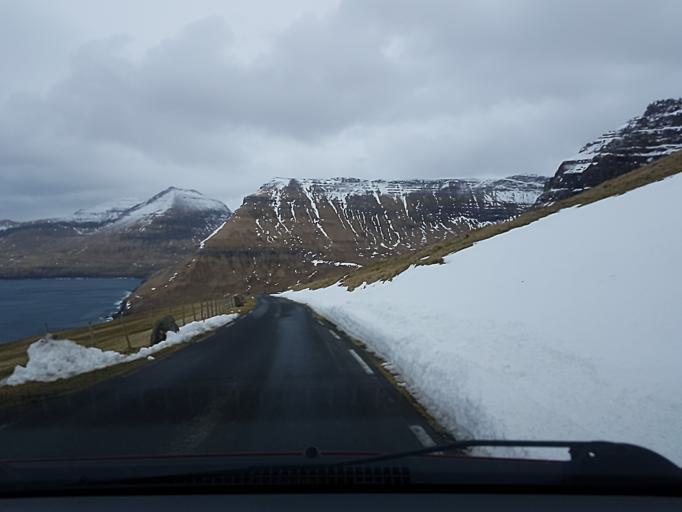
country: FO
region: Streymoy
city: Kollafjordhur
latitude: 62.0124
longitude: -6.9096
